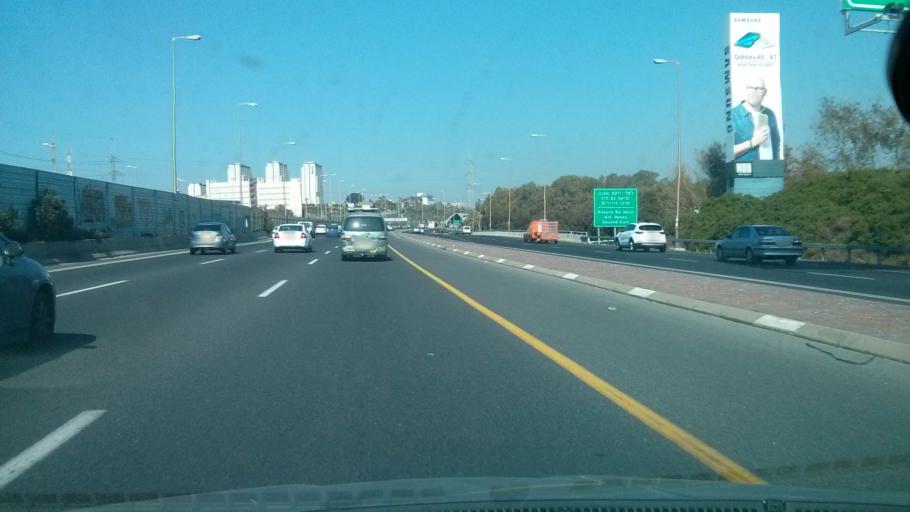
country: IL
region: Tel Aviv
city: Ramat Gan
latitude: 32.0980
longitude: 34.8026
